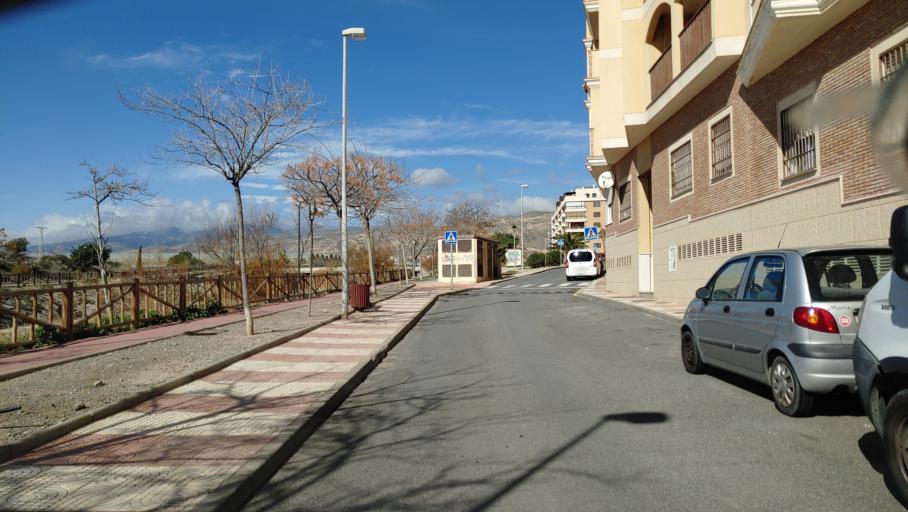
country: ES
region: Andalusia
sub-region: Provincia de Almeria
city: Aguadulce
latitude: 36.8005
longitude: -2.5849
